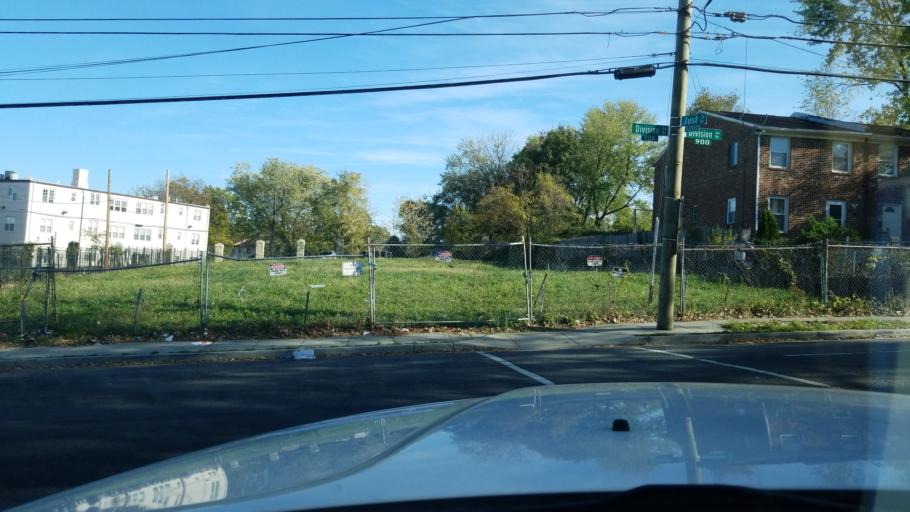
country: US
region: Maryland
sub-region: Prince George's County
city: Fairmount Heights
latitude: 38.9028
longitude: -76.9241
